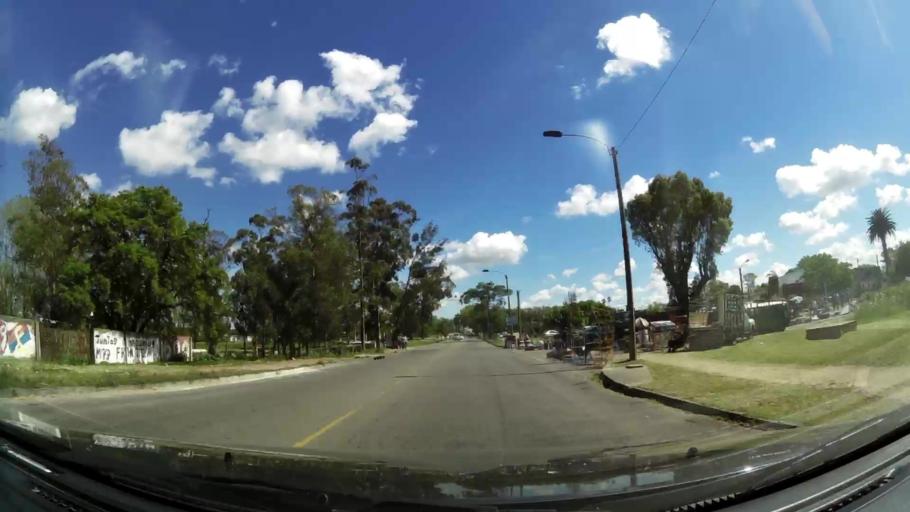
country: UY
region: Montevideo
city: Montevideo
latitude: -34.8359
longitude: -56.1396
